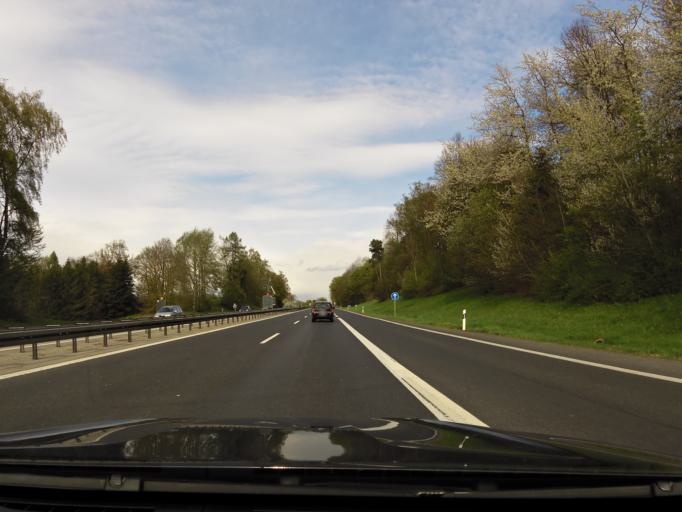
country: DE
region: Bavaria
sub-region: Upper Bavaria
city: Wolnzach
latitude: 48.5971
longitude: 11.6356
